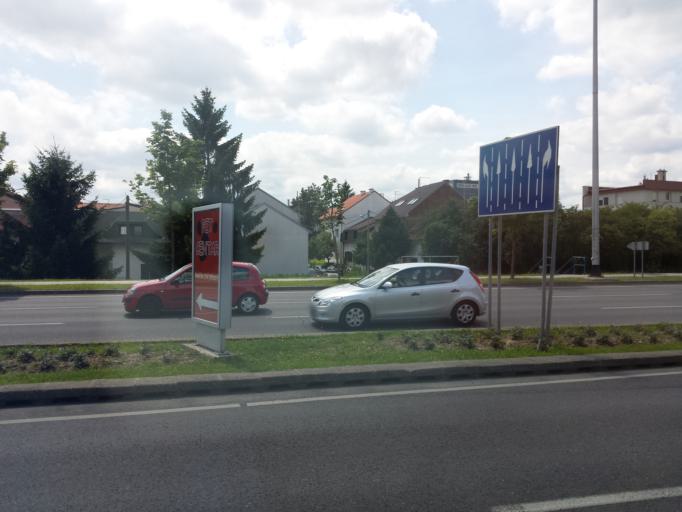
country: HR
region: Grad Zagreb
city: Jankomir
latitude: 45.7941
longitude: 15.9336
